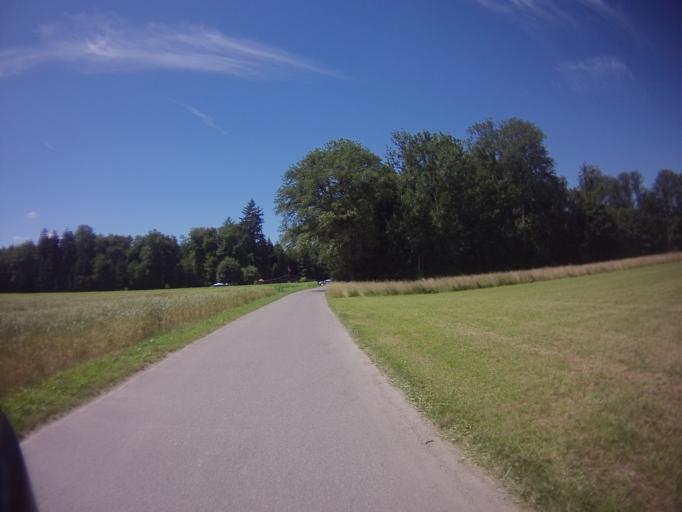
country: CH
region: Bern
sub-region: Emmental District
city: Kirchberg
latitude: 47.0790
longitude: 7.5654
